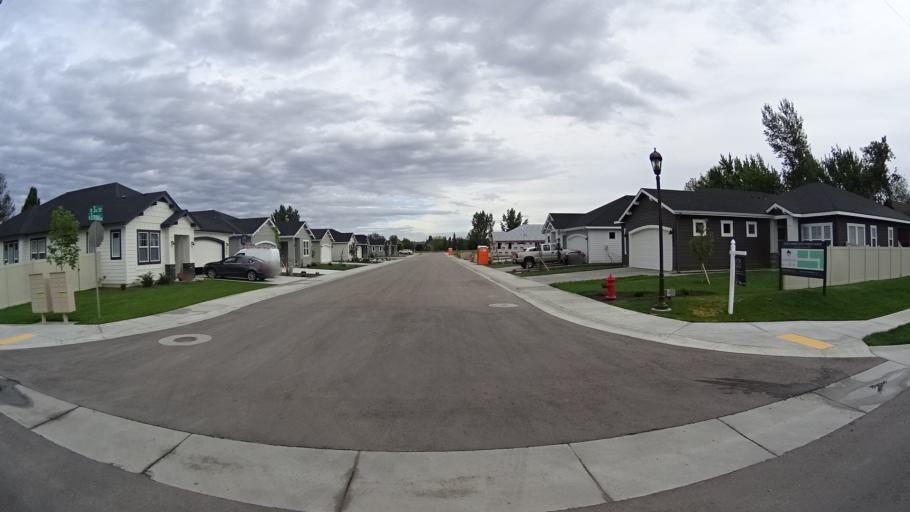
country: US
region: Idaho
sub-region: Ada County
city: Star
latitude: 43.6957
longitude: -116.4975
